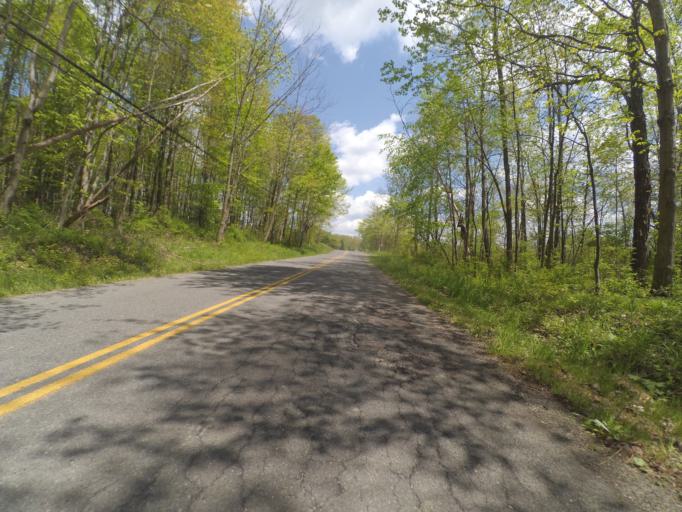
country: US
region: Ohio
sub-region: Portage County
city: Ravenna
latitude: 41.1193
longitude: -81.1560
